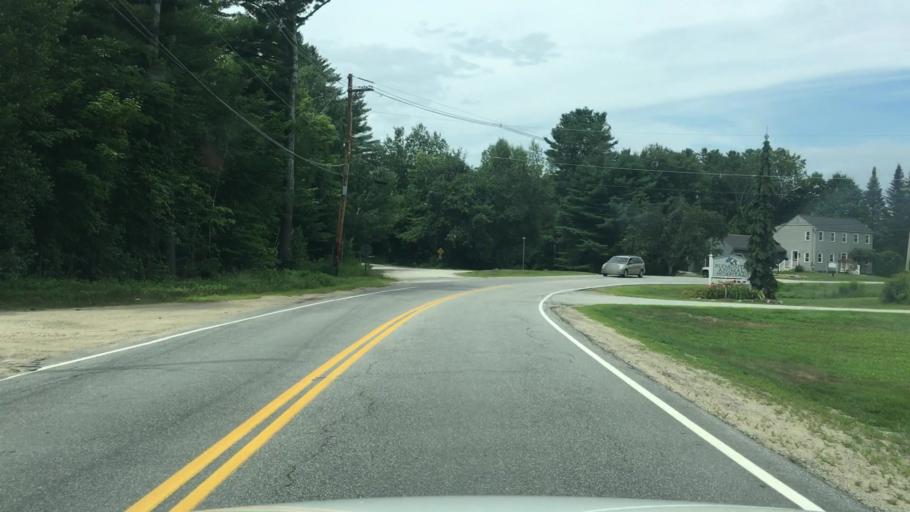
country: US
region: New Hampshire
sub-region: Grafton County
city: Plymouth
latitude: 43.7721
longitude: -71.7339
